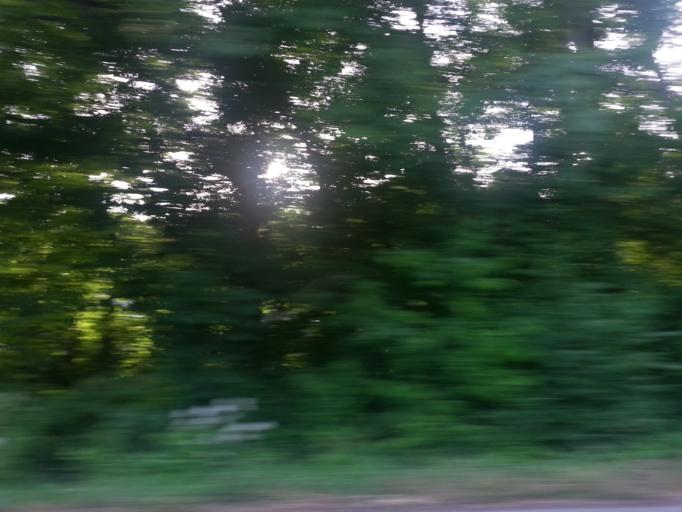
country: US
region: Tennessee
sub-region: Sevier County
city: Seymour
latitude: 35.8608
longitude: -83.7923
